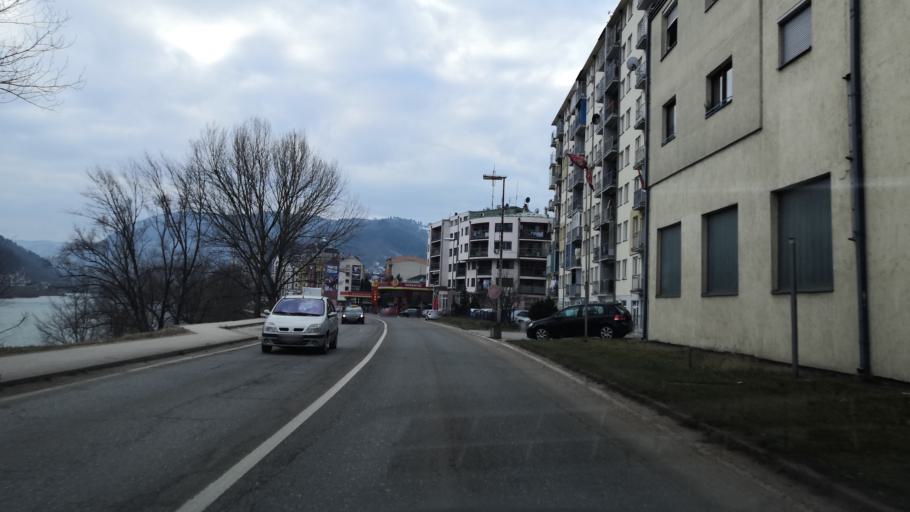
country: BA
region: Republika Srpska
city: Zvornik
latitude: 44.3946
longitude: 19.1066
